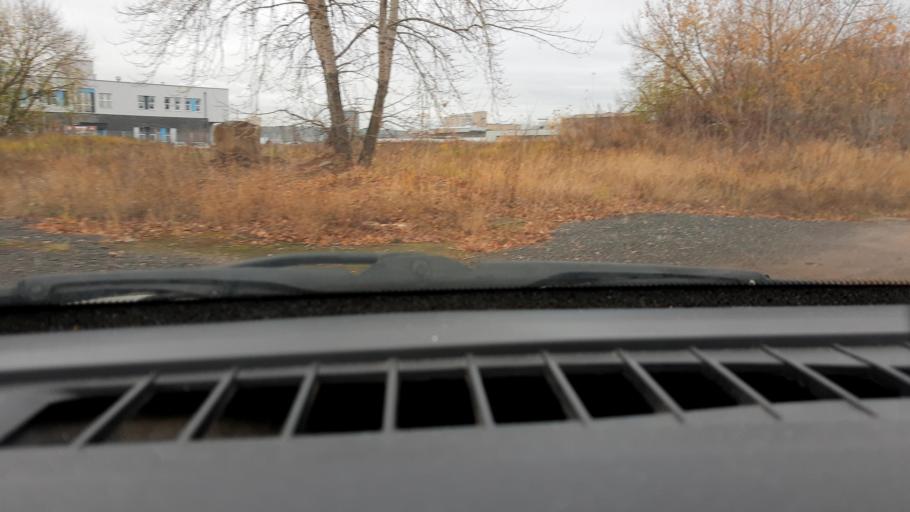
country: RU
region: Nizjnij Novgorod
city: Nizhniy Novgorod
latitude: 56.3097
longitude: 43.9554
